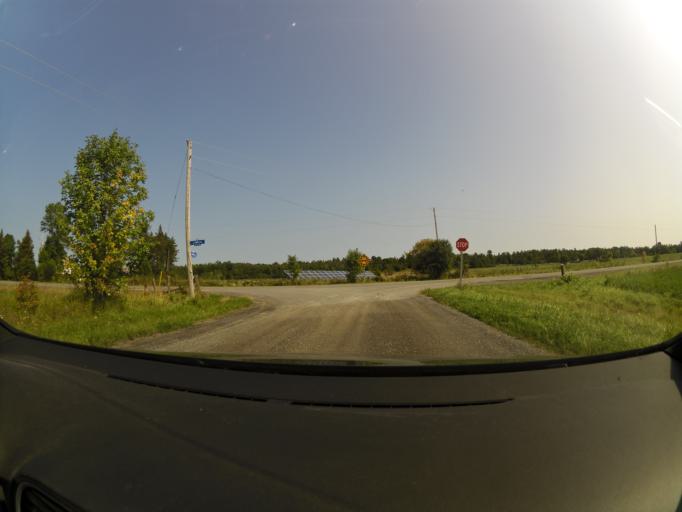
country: CA
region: Ontario
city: Arnprior
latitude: 45.4998
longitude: -76.2053
